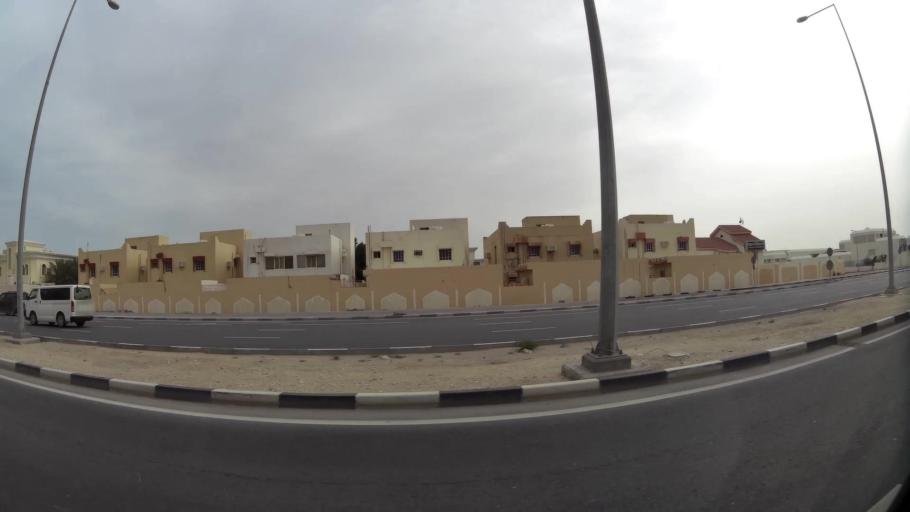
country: QA
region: Baladiyat ad Dawhah
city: Doha
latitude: 25.3350
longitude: 51.4868
